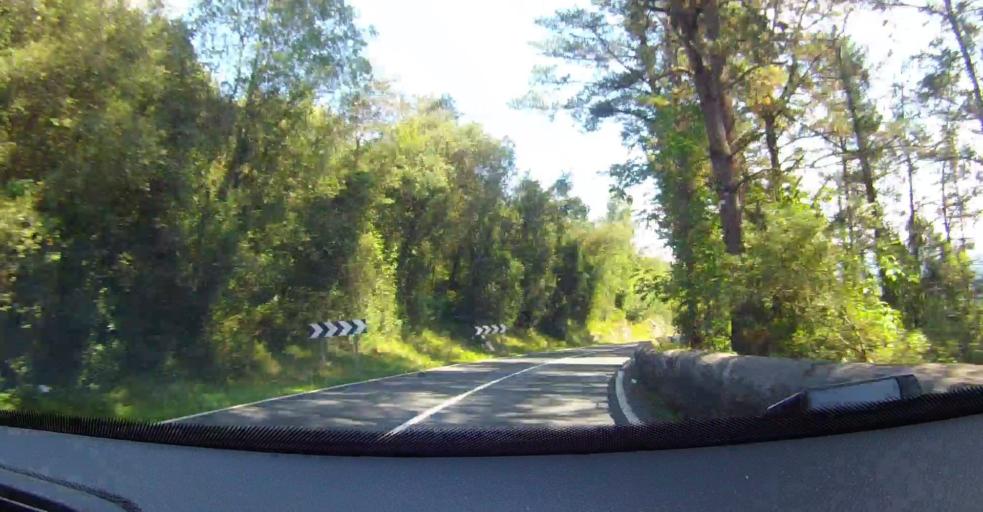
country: ES
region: Basque Country
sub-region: Bizkaia
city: Kortezubi
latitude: 43.3624
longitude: -2.6534
